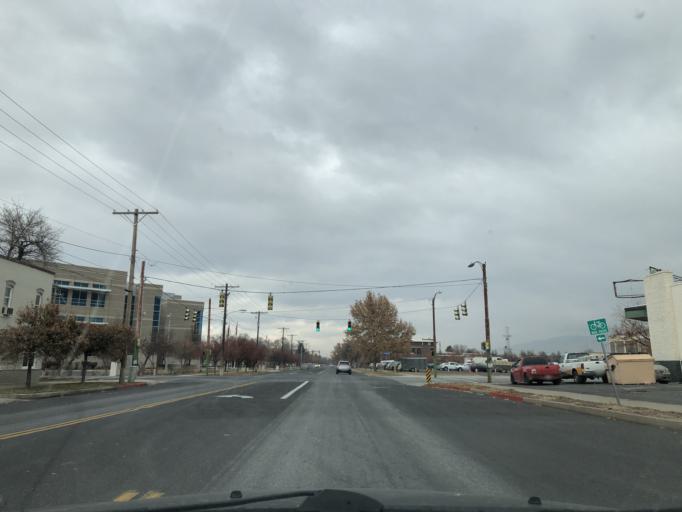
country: US
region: Utah
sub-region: Cache County
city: Logan
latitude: 41.7328
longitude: -111.8375
